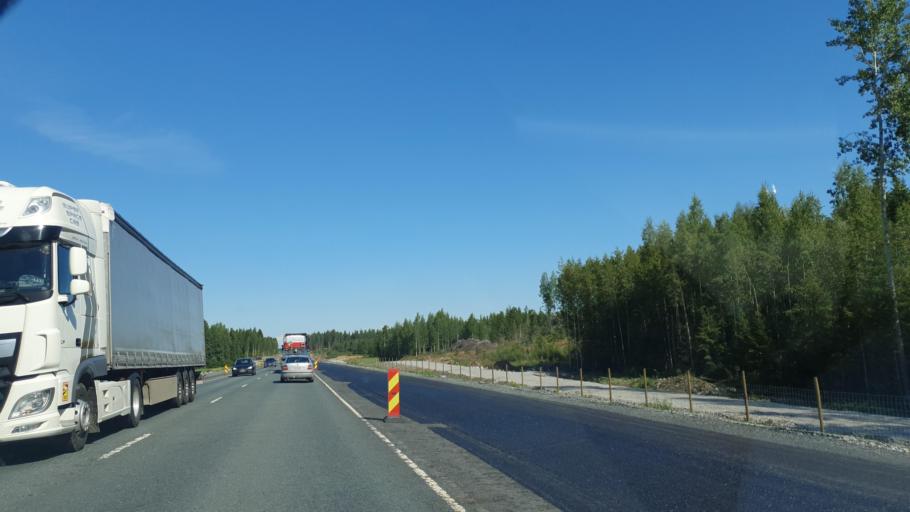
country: FI
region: Northern Savo
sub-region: Ylae-Savo
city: Lapinlahti
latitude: 63.2953
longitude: 27.4531
